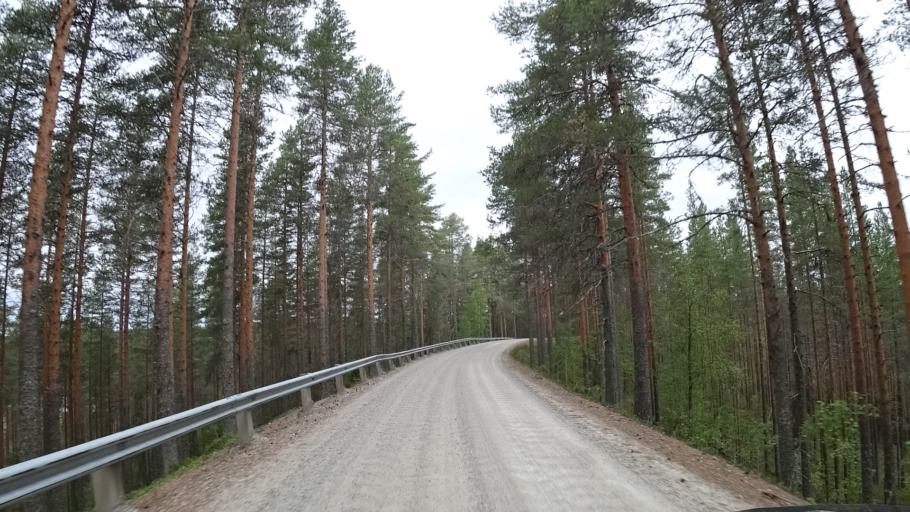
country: FI
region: North Karelia
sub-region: Pielisen Karjala
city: Lieksa
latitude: 63.2127
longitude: 30.4118
